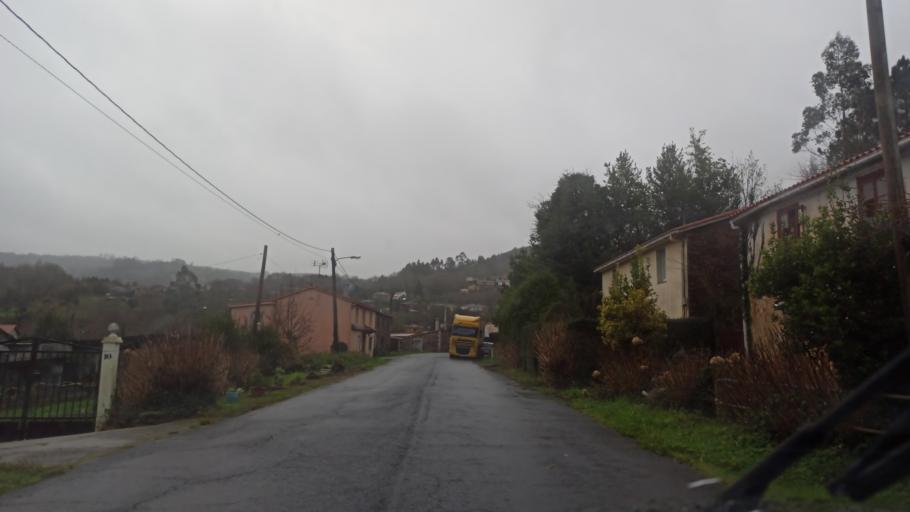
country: ES
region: Galicia
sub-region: Provincia da Coruna
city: Cesuras
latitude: 43.1766
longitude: -8.1754
